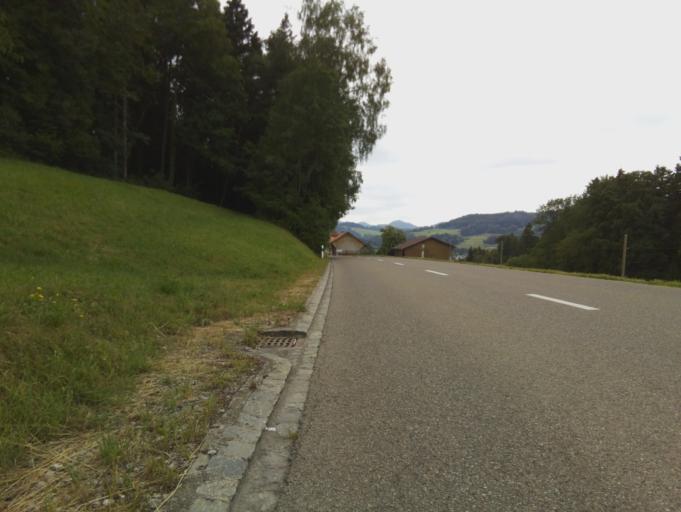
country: CH
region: Saint Gallen
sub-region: Wahlkreis Wil
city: Jonschwil
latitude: 47.4161
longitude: 9.0846
